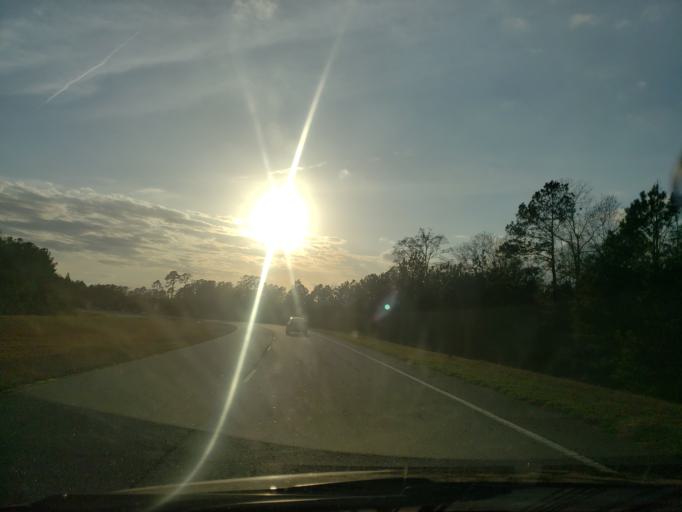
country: US
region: Georgia
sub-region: Chatham County
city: Bloomingdale
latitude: 32.1462
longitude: -81.3044
